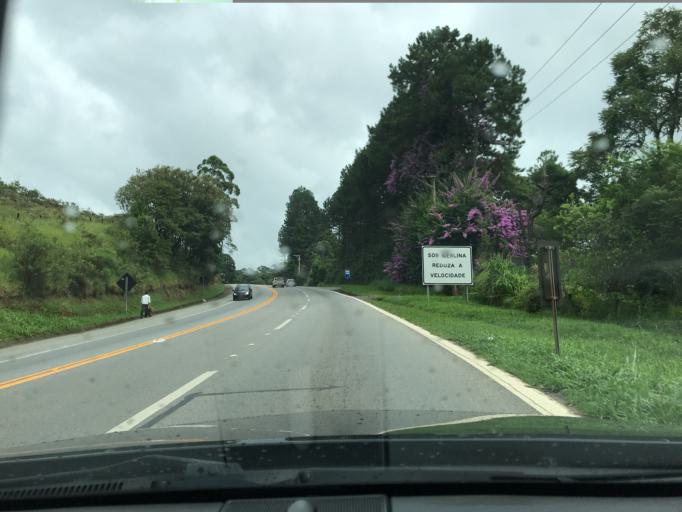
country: BR
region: Sao Paulo
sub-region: Vargem Grande Paulista
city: Vargem Grande Paulista
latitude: -23.5958
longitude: -47.0555
